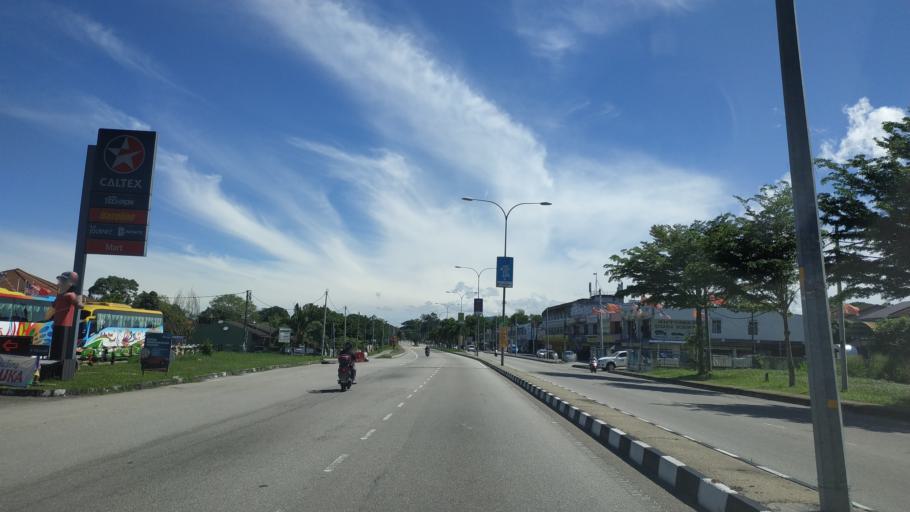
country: MY
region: Kedah
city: Kulim
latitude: 5.3613
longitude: 100.5468
